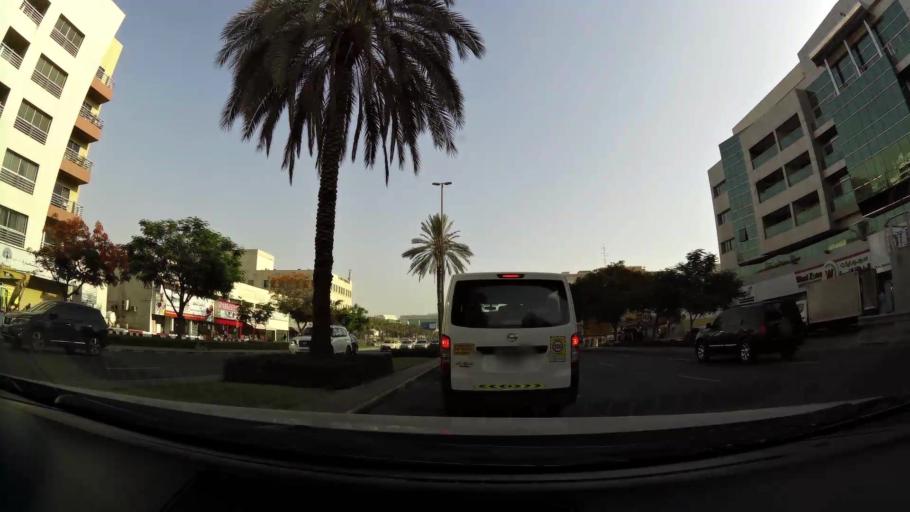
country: AE
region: Ash Shariqah
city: Sharjah
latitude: 25.2469
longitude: 55.3082
